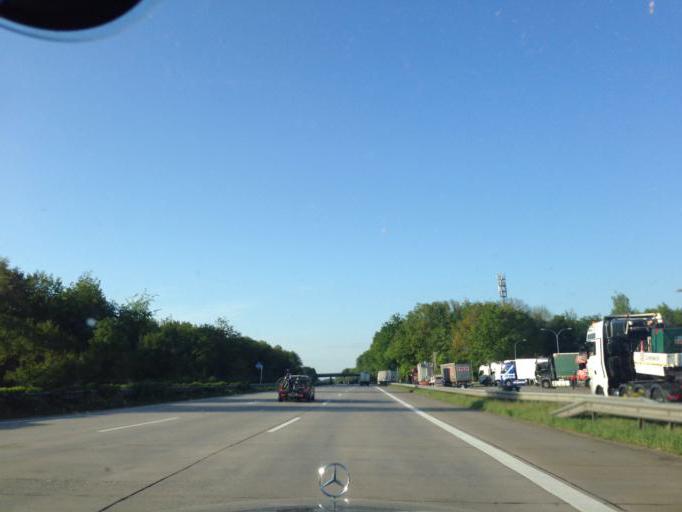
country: DE
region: Schleswig-Holstein
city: Hammoor
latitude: 53.6932
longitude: 10.3223
